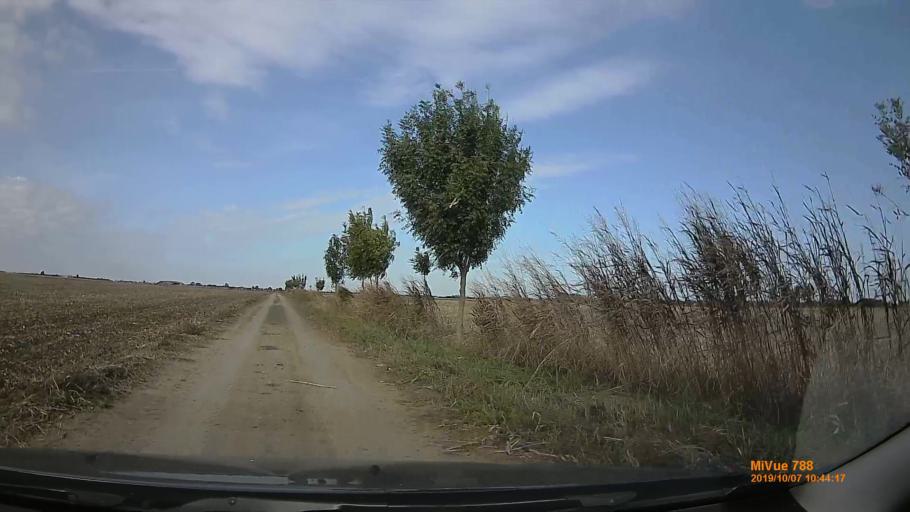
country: HU
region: Bekes
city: Kondoros
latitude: 46.7331
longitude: 20.8322
